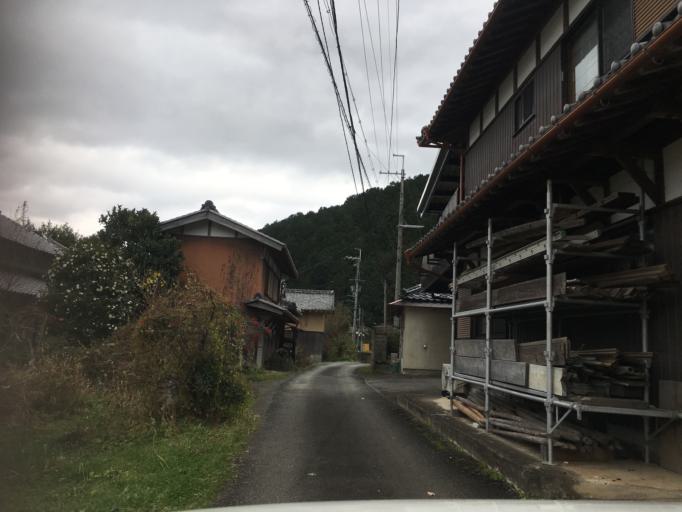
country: JP
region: Kyoto
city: Kameoka
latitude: 35.0390
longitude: 135.4767
